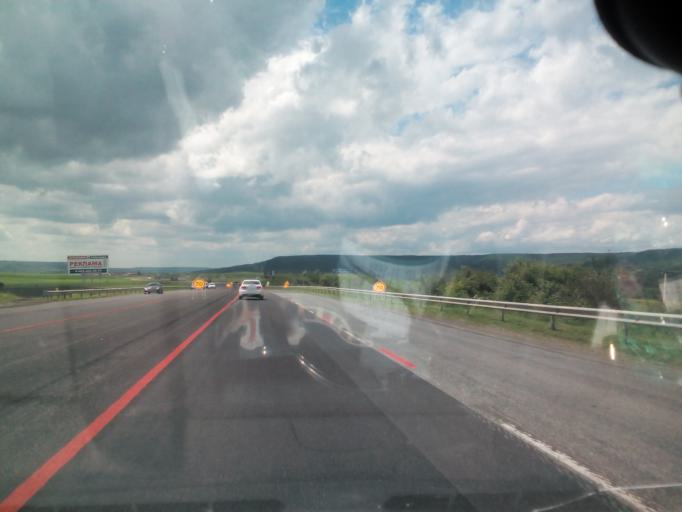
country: RU
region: Stavropol'skiy
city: Tatarka
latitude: 44.9516
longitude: 41.9442
